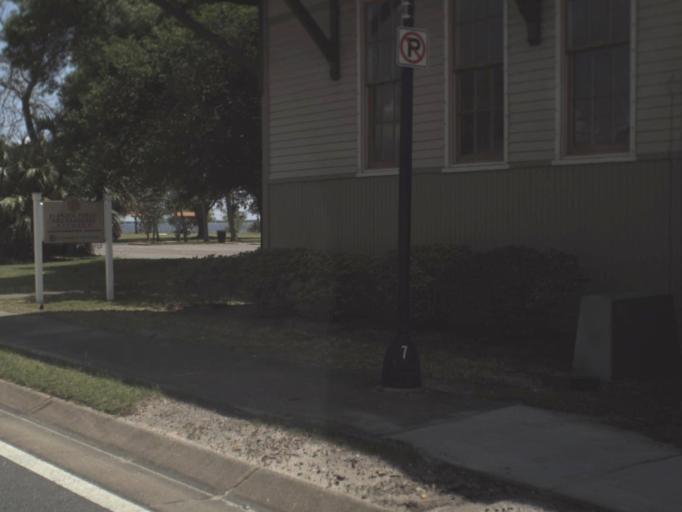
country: US
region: Florida
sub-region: Escambia County
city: Pensacola
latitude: 30.4082
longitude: -87.2106
